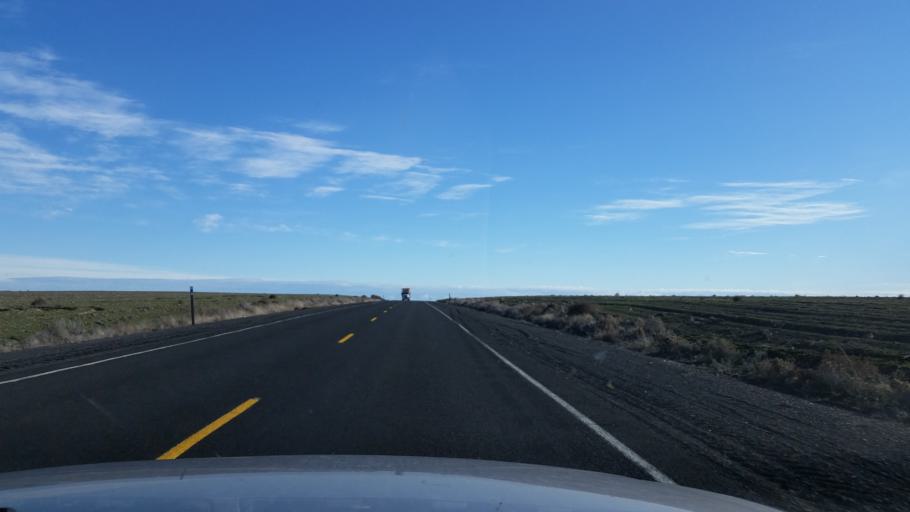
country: US
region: Washington
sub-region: Grant County
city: Warden
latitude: 47.3525
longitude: -118.9414
